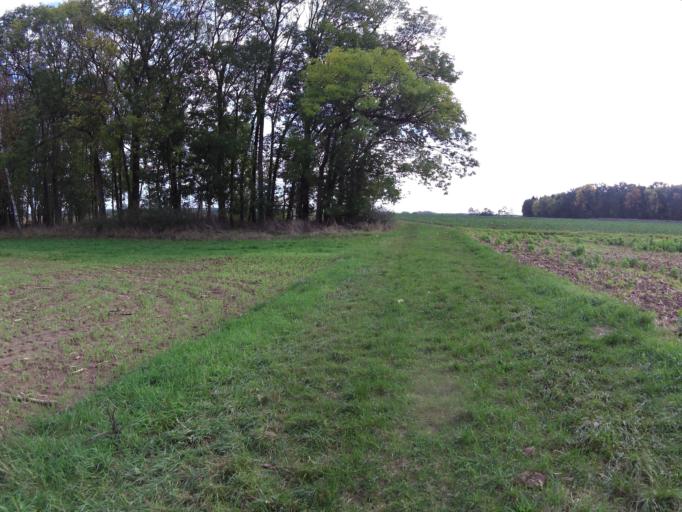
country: DE
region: Bavaria
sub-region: Regierungsbezirk Unterfranken
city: Biebelried
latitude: 49.7324
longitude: 10.0694
